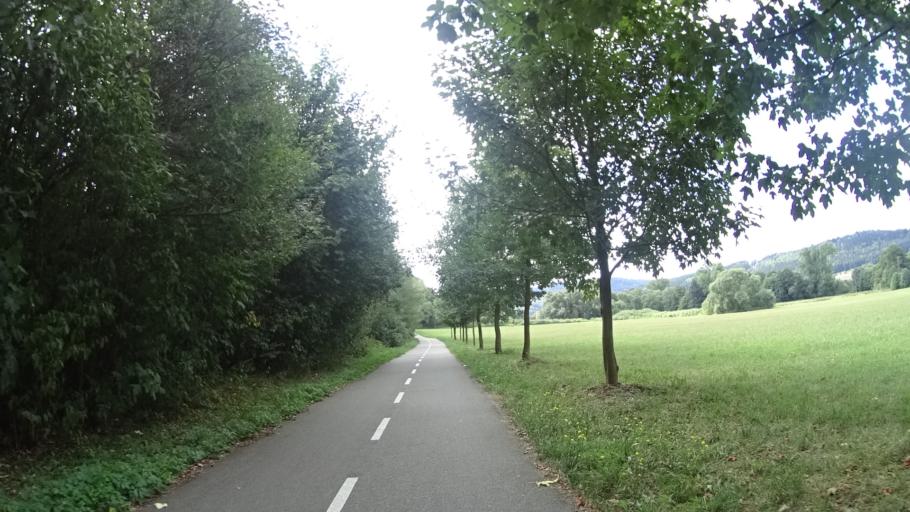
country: CZ
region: Pardubicky
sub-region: Okres Usti nad Orlici
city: Usti nad Orlici
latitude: 49.9874
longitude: 16.3950
